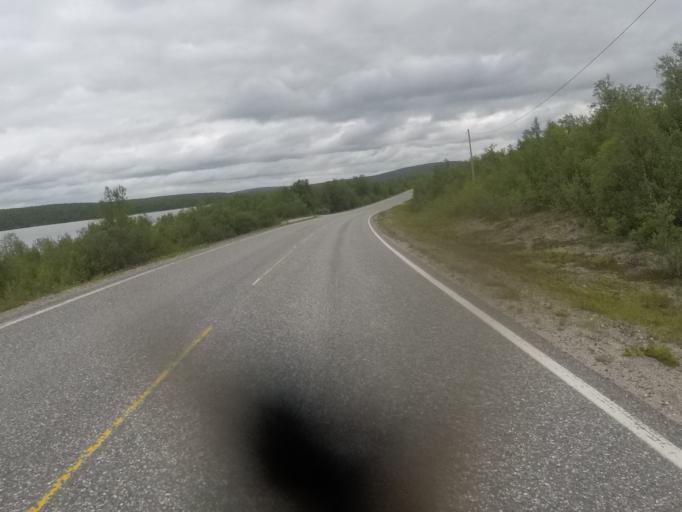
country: NO
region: Finnmark Fylke
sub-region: Kautokeino
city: Kautokeino
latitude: 68.9497
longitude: 23.0886
